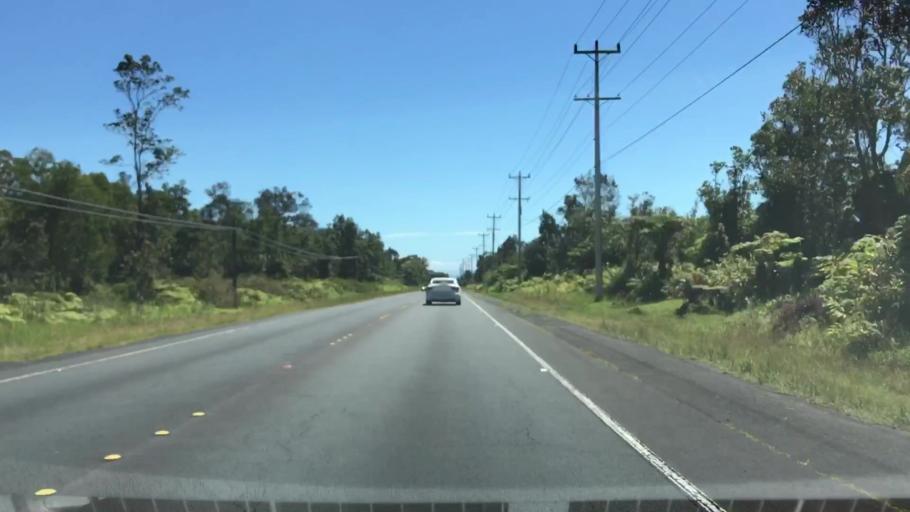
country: US
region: Hawaii
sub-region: Hawaii County
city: Volcano
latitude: 19.4535
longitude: -155.1806
